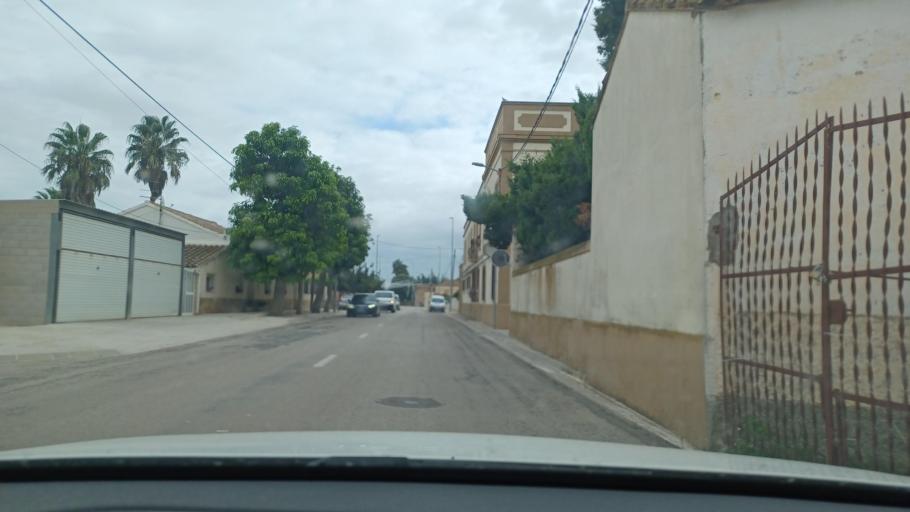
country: ES
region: Catalonia
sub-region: Provincia de Tarragona
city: Deltebre
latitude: 40.7249
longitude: 0.6888
